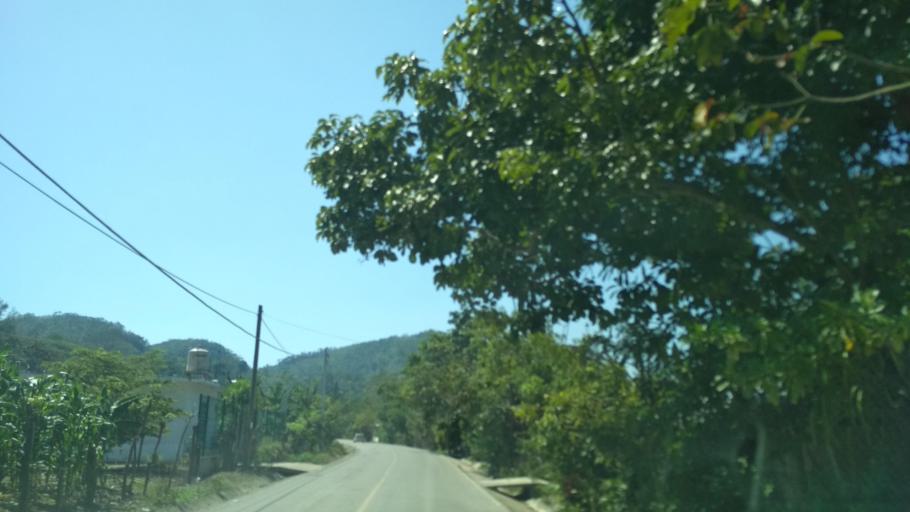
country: MX
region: Veracruz
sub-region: Papantla
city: Polutla
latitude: 20.4784
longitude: -97.2049
